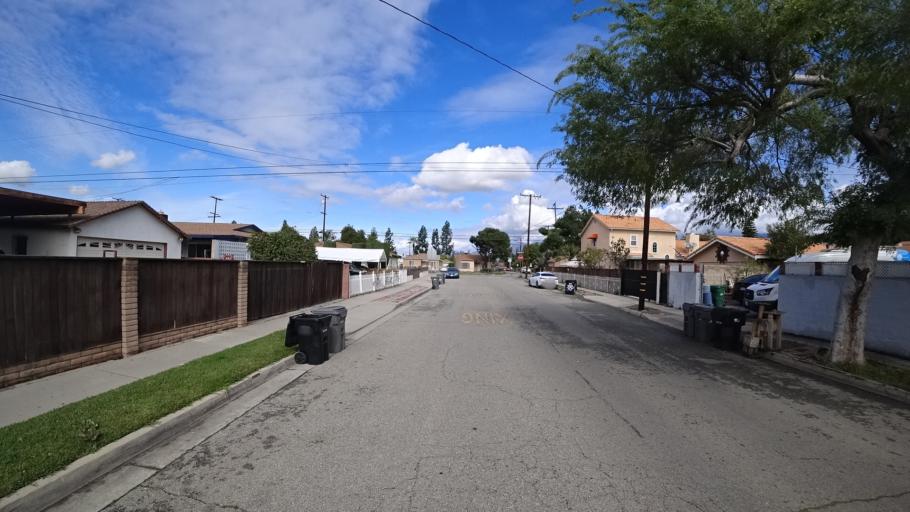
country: US
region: California
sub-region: Los Angeles County
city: Baldwin Park
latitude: 34.0812
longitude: -117.9643
